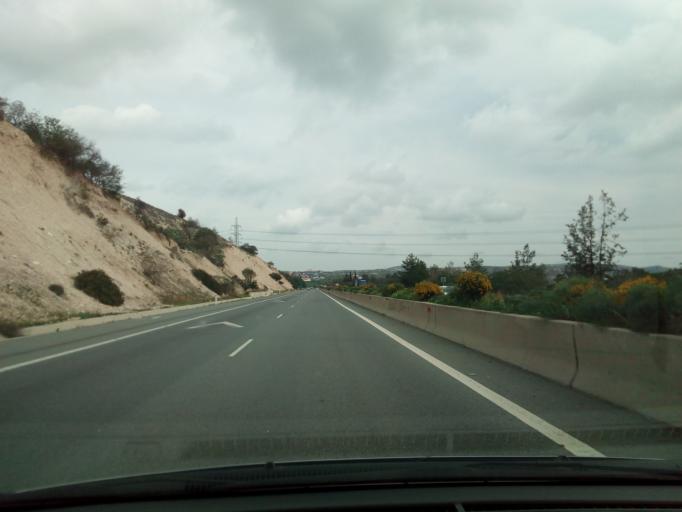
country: CY
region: Lefkosia
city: Dali
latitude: 34.9981
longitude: 33.4278
